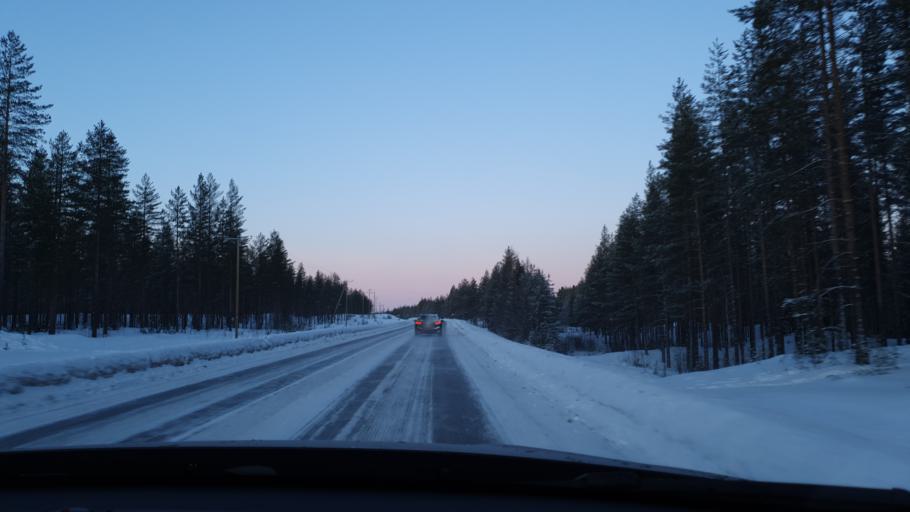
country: FI
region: Kainuu
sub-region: Kajaani
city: Sotkamo
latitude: 64.0828
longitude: 28.6049
